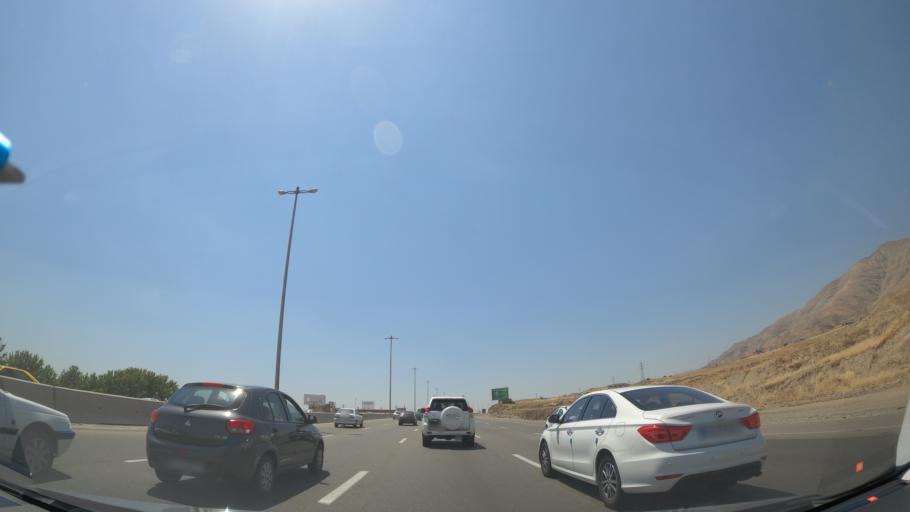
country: IR
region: Tehran
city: Shahr-e Qods
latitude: 35.7451
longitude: 51.0921
